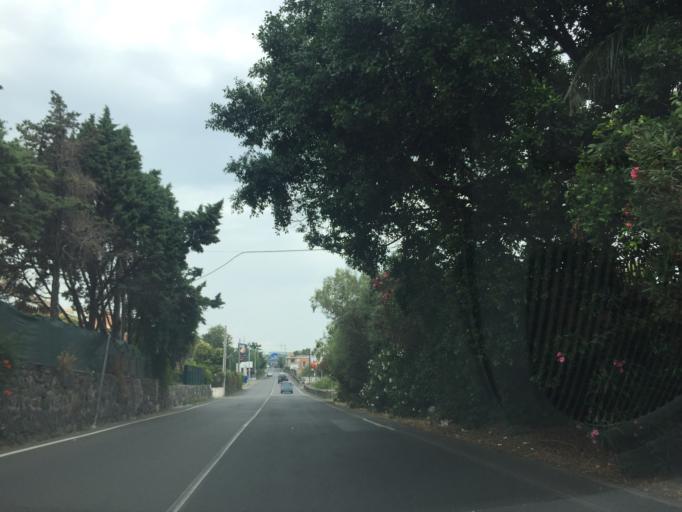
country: IT
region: Sicily
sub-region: Catania
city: Vambolieri
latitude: 37.5742
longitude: 15.1674
